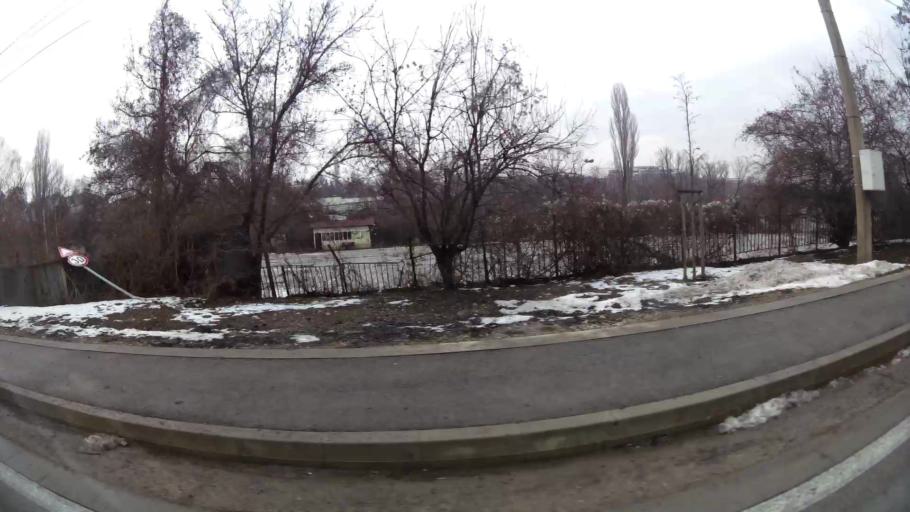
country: BG
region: Sofia-Capital
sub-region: Stolichna Obshtina
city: Sofia
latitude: 42.6702
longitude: 23.2433
